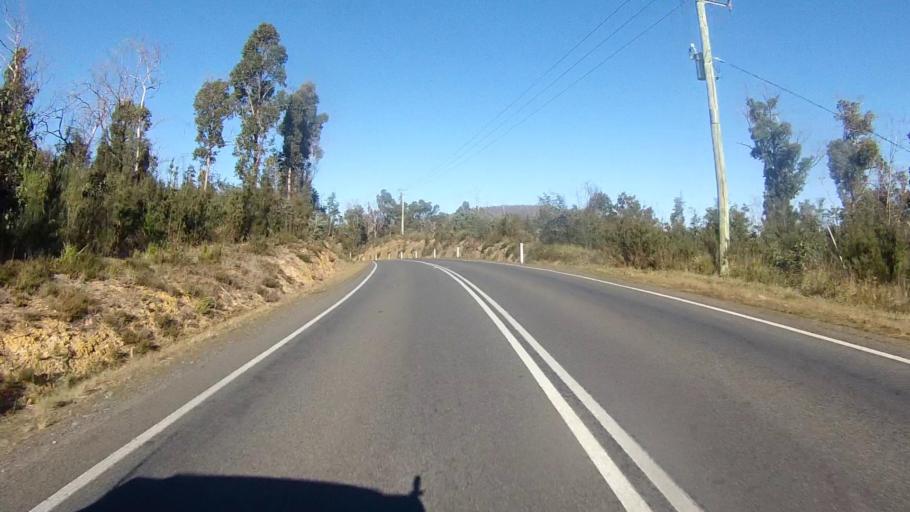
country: AU
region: Tasmania
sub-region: Sorell
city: Sorell
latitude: -42.8311
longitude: 147.8074
